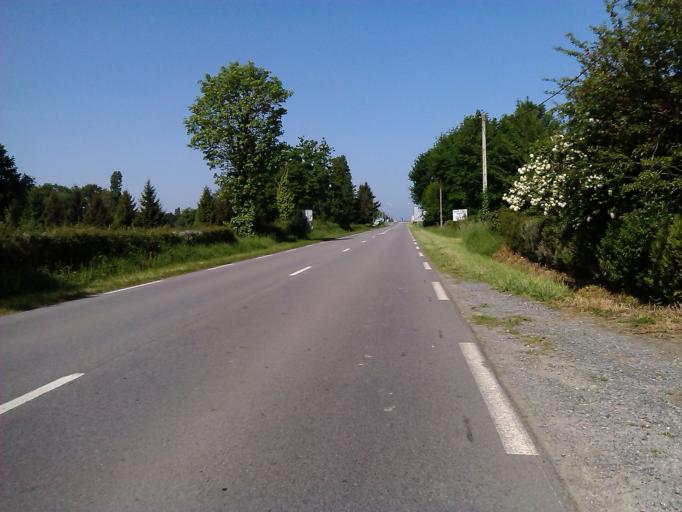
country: FR
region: Centre
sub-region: Departement de l'Indre
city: Neuvy-Saint-Sepulchre
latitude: 46.5985
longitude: 1.7802
